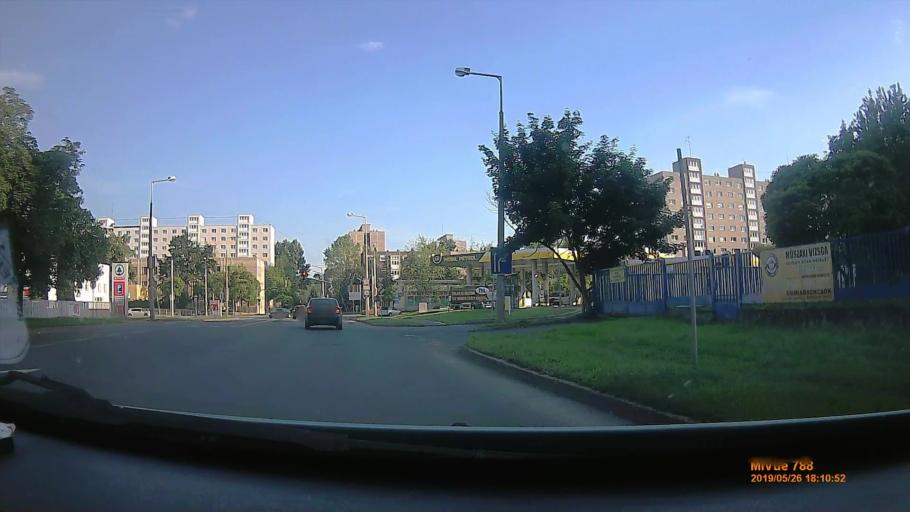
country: HU
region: Borsod-Abauj-Zemplen
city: Miskolc
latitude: 48.1048
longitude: 20.7572
